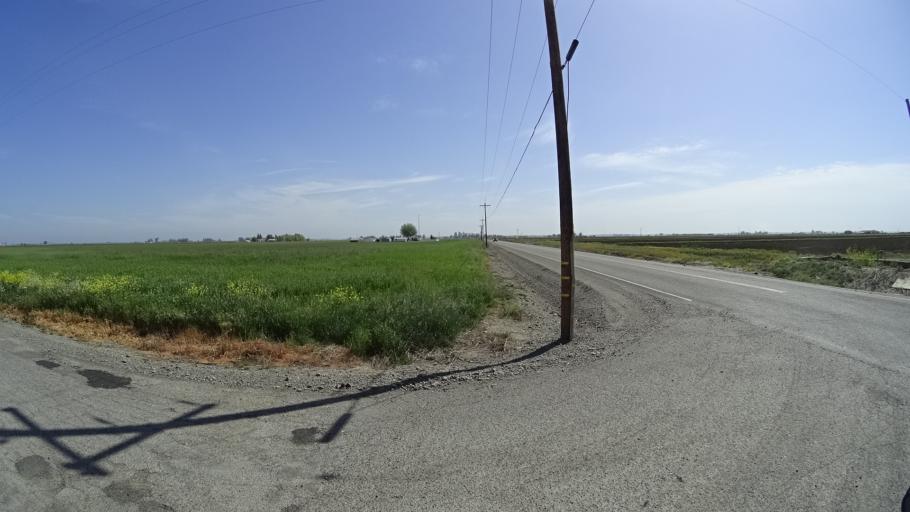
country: US
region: California
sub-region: Glenn County
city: Willows
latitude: 39.5829
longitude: -122.0887
